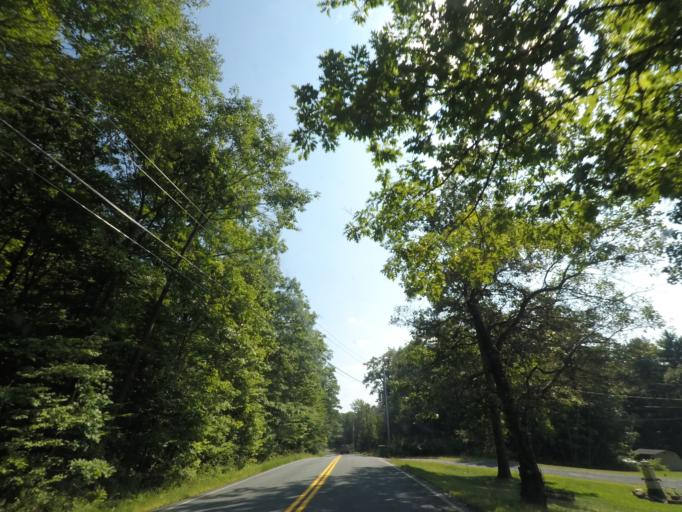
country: US
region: New York
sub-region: Rensselaer County
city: Poestenkill
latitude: 42.7263
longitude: -73.5100
